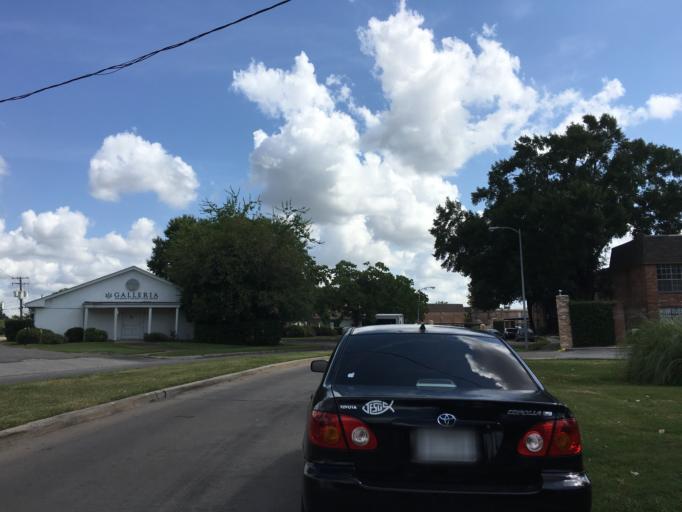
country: US
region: Texas
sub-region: Harris County
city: Piney Point Village
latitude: 29.7350
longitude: -95.5057
